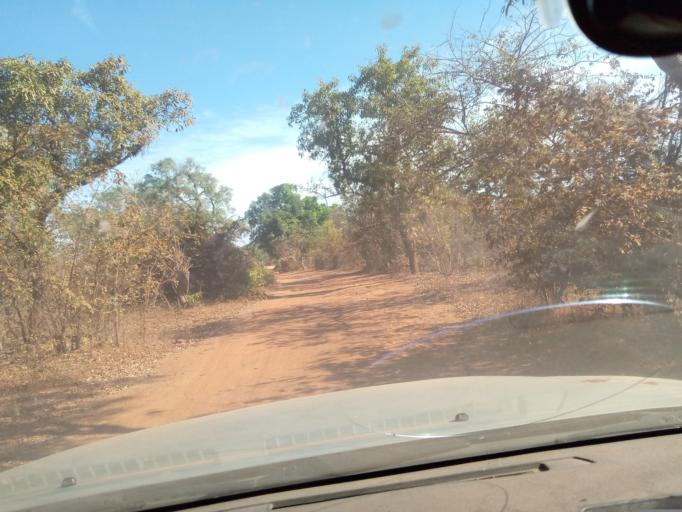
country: ML
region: Sikasso
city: Sikasso
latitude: 11.4695
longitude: -5.3281
